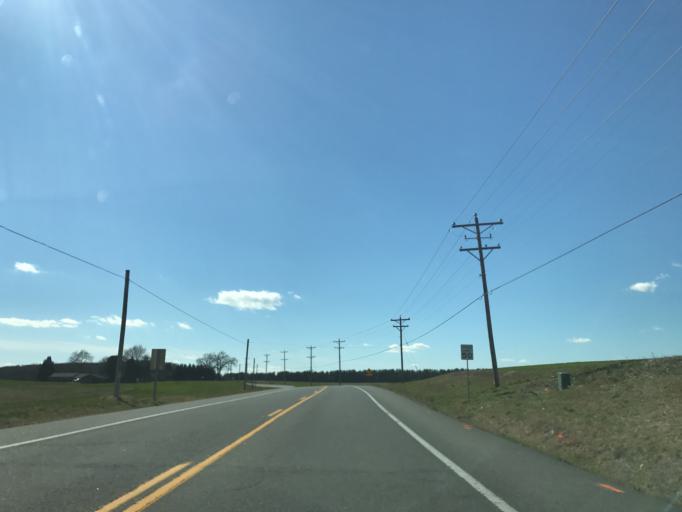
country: US
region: Maryland
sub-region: Kent County
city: Chestertown
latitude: 39.2169
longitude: -76.0884
